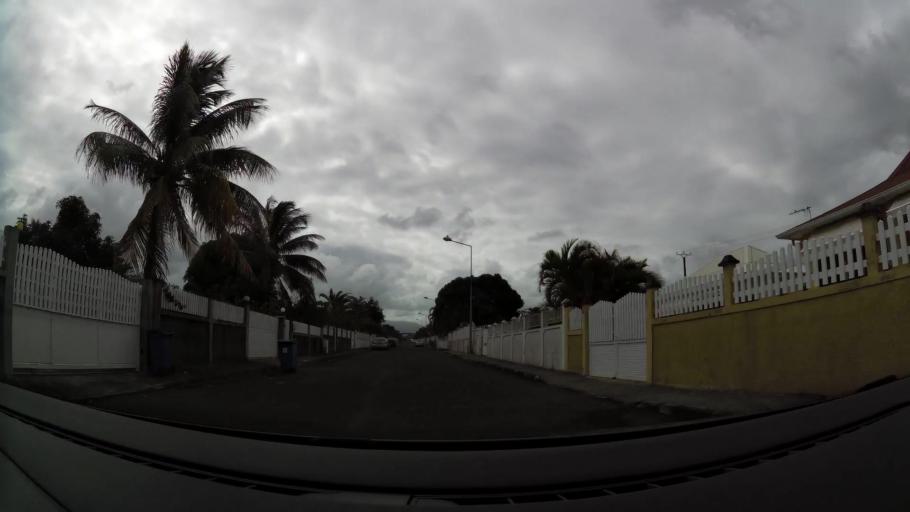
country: GP
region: Guadeloupe
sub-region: Guadeloupe
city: Lamentin
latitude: 16.2633
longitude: -61.6247
